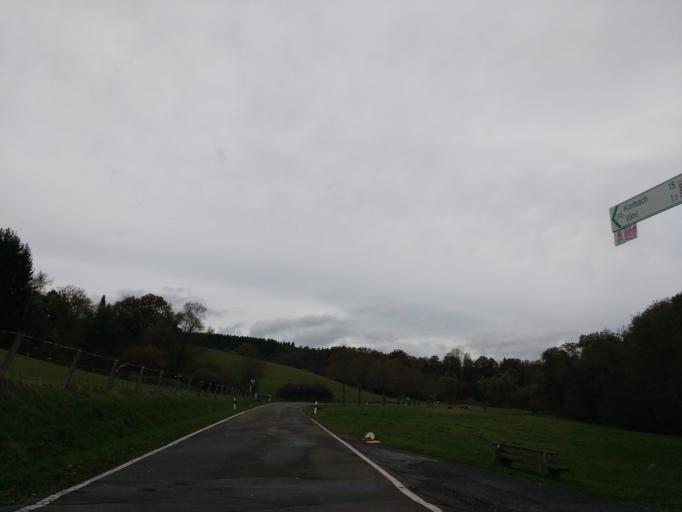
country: DE
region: Hesse
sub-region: Regierungsbezirk Kassel
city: Vohl
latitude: 51.1934
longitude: 8.9510
